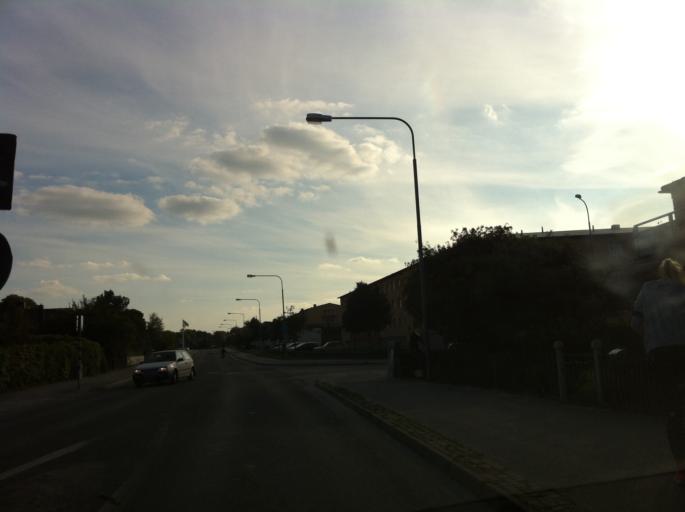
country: SE
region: Gotland
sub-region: Gotland
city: Visby
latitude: 57.6239
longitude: 18.2853
